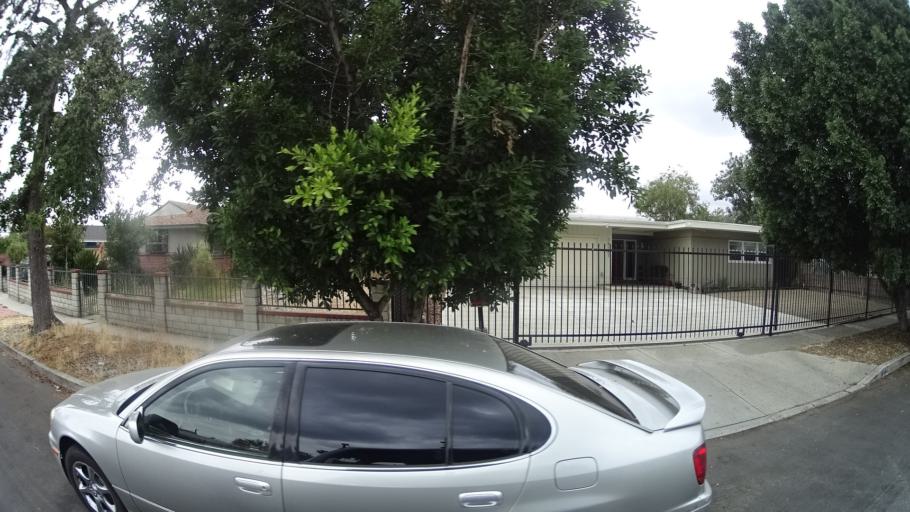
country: US
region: California
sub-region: Los Angeles County
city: San Fernando
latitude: 34.2528
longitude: -118.4421
